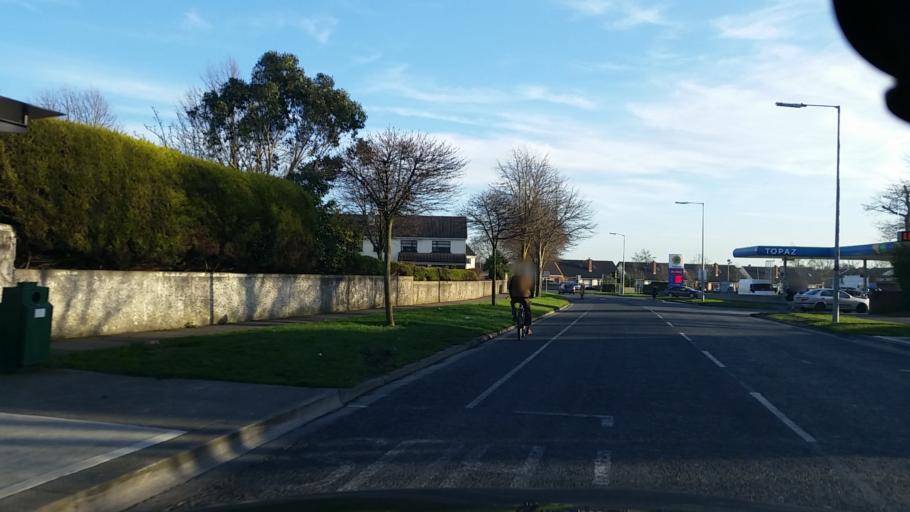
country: IE
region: Leinster
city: Hartstown
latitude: 53.3935
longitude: -6.4186
